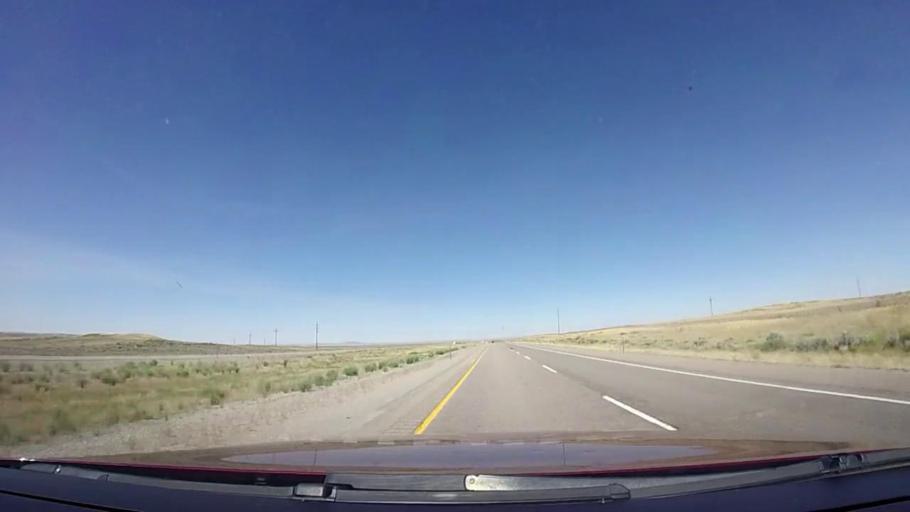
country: US
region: Wyoming
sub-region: Sweetwater County
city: Rock Springs
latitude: 41.6327
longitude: -108.3633
